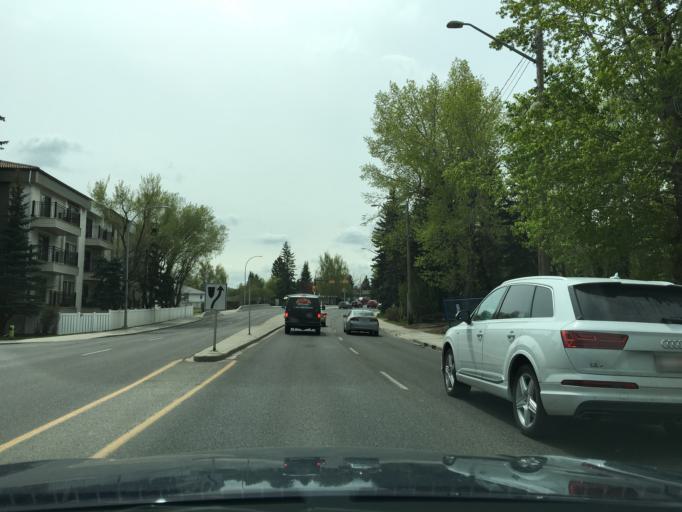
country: CA
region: Alberta
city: Calgary
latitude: 51.0027
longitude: -114.0814
